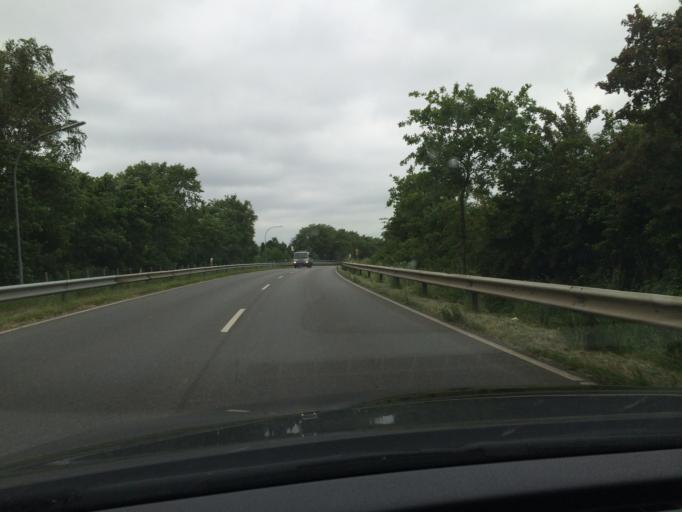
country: DE
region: Schleswig-Holstein
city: Kolln-Reisiek
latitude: 53.7781
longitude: 9.7077
